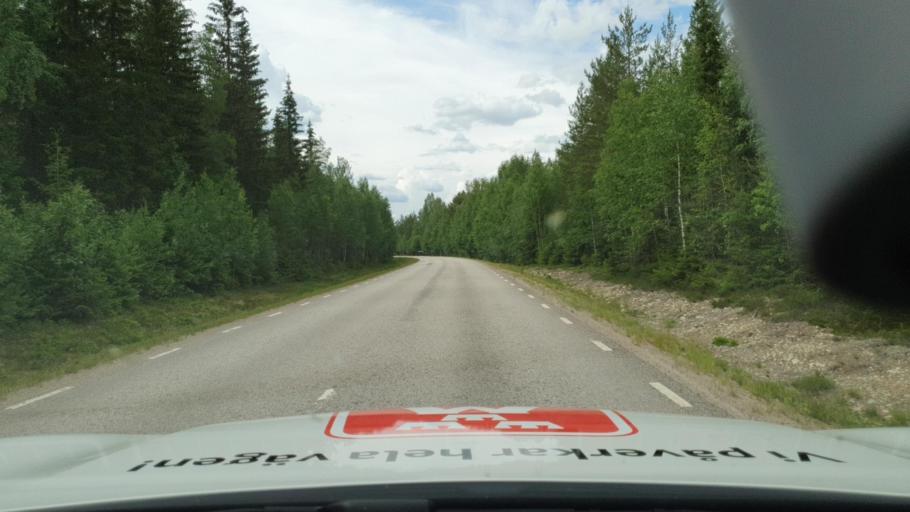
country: NO
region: Hedmark
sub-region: Trysil
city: Innbygda
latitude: 60.9083
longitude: 12.5603
